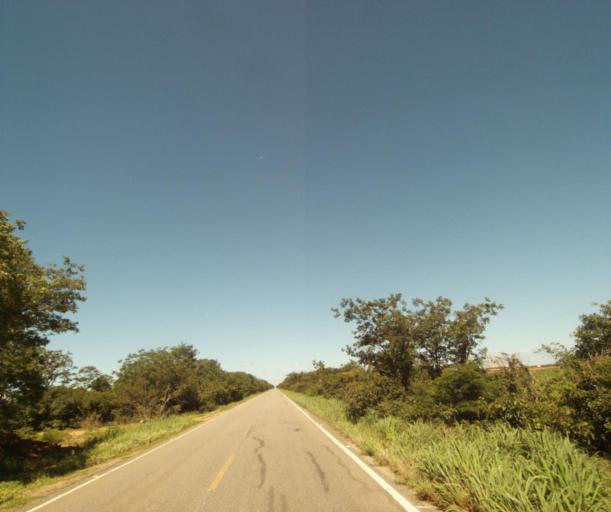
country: BR
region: Bahia
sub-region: Carinhanha
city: Carinhanha
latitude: -14.2827
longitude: -43.5609
